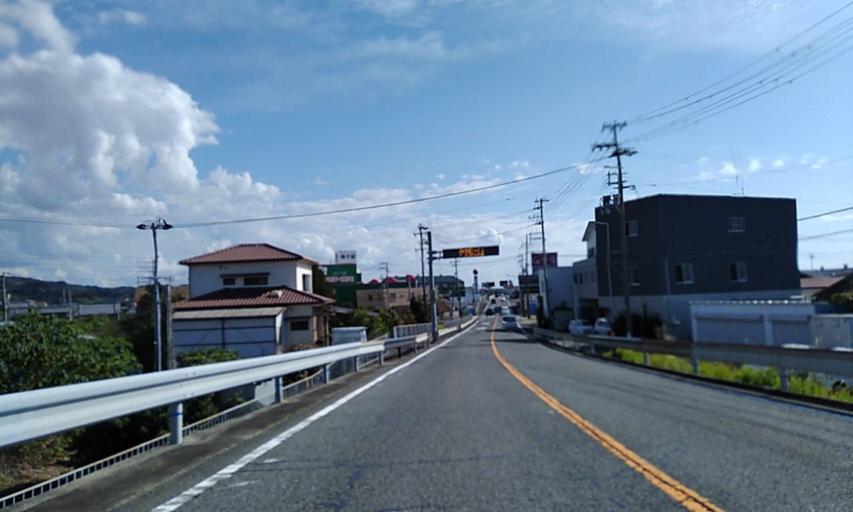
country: JP
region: Wakayama
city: Tanabe
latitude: 33.7742
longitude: 135.3124
